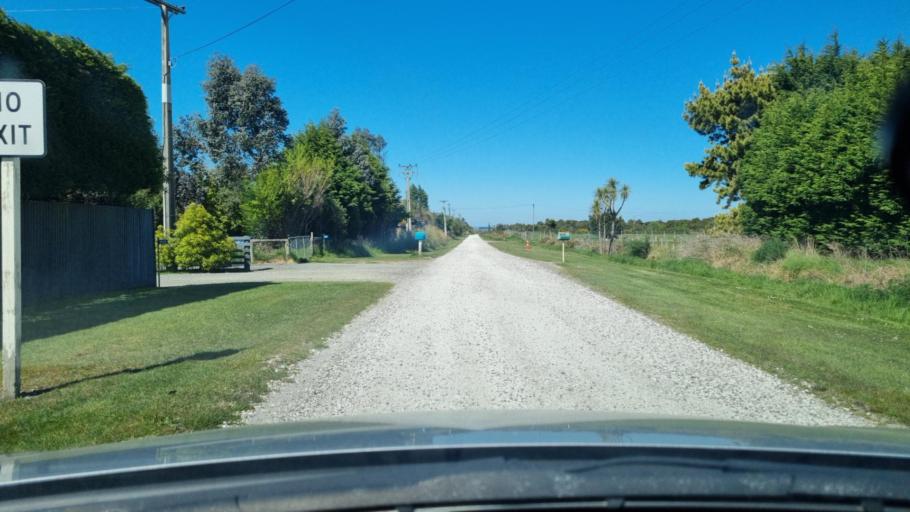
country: NZ
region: Southland
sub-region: Invercargill City
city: Invercargill
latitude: -46.4482
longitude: 168.3166
